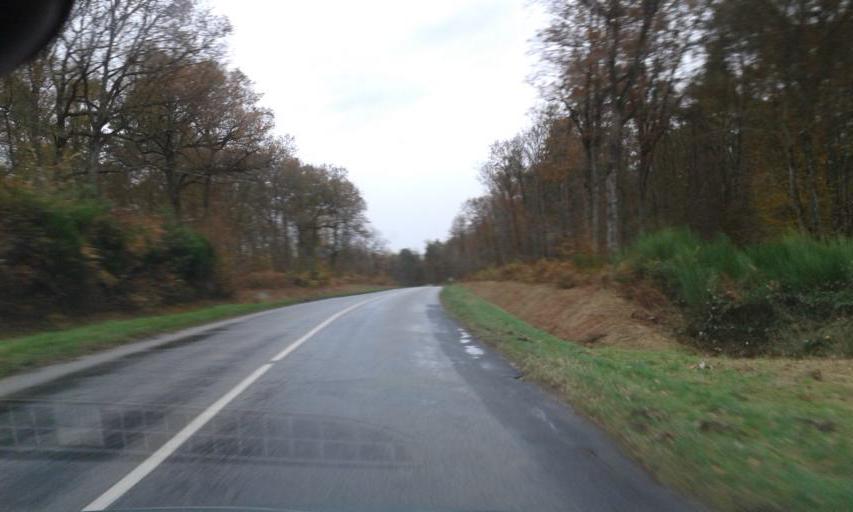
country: FR
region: Centre
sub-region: Departement du Loiret
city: Vitry-aux-Loges
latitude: 47.9147
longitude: 2.2543
